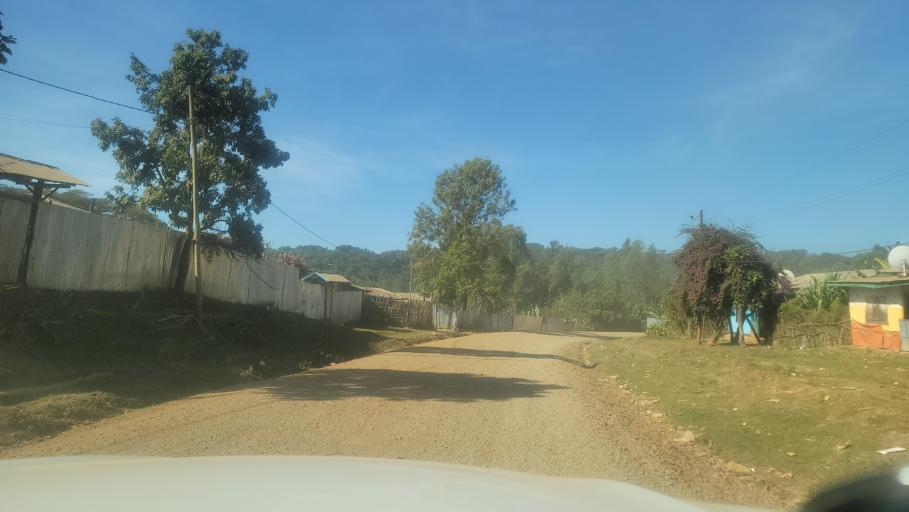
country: ET
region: Oromiya
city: Agaro
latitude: 7.8146
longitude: 36.5151
